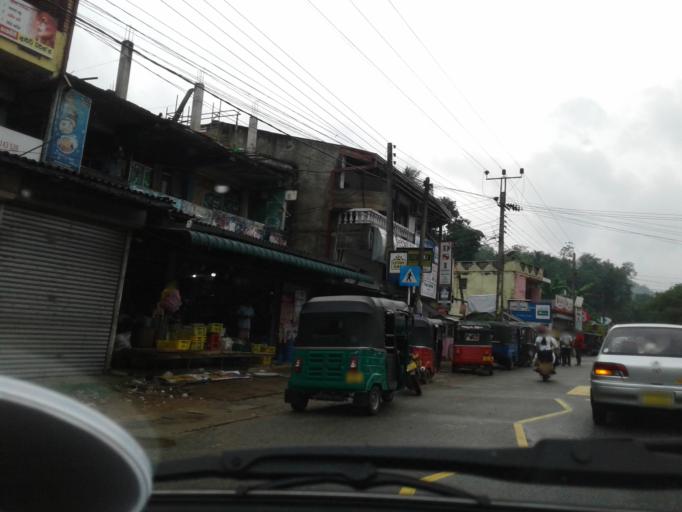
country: LK
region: Central
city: Kadugannawa
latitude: 7.2348
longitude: 80.2629
